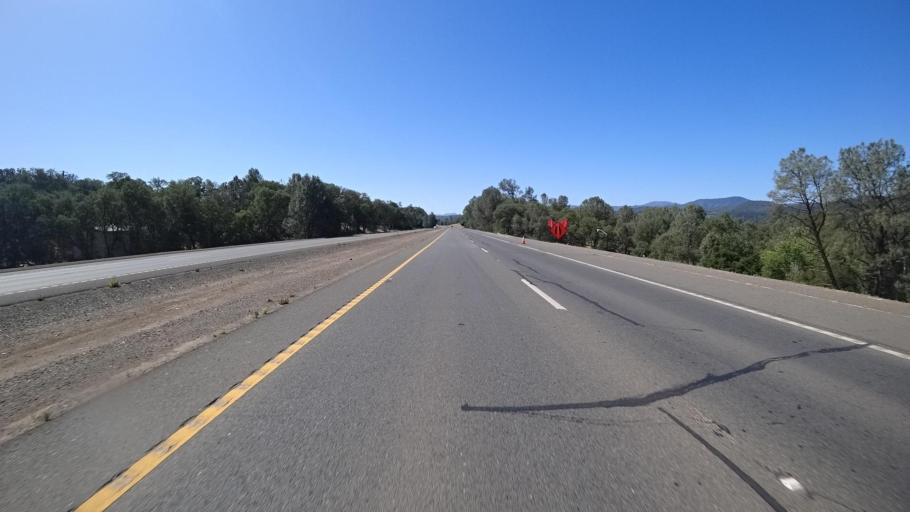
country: US
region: California
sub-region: Lake County
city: Clearlake
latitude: 38.9464
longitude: -122.6234
